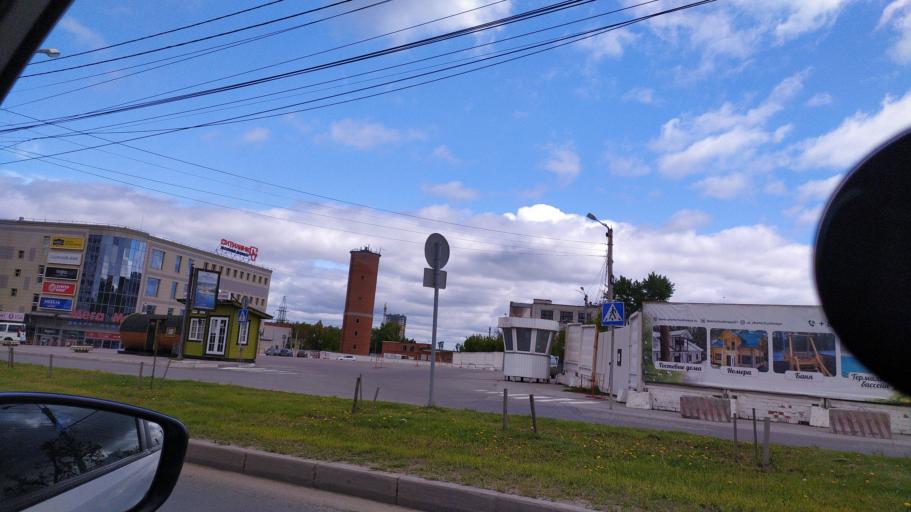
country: RU
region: Chuvashia
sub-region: Cheboksarskiy Rayon
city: Cheboksary
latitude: 56.1356
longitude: 47.2797
